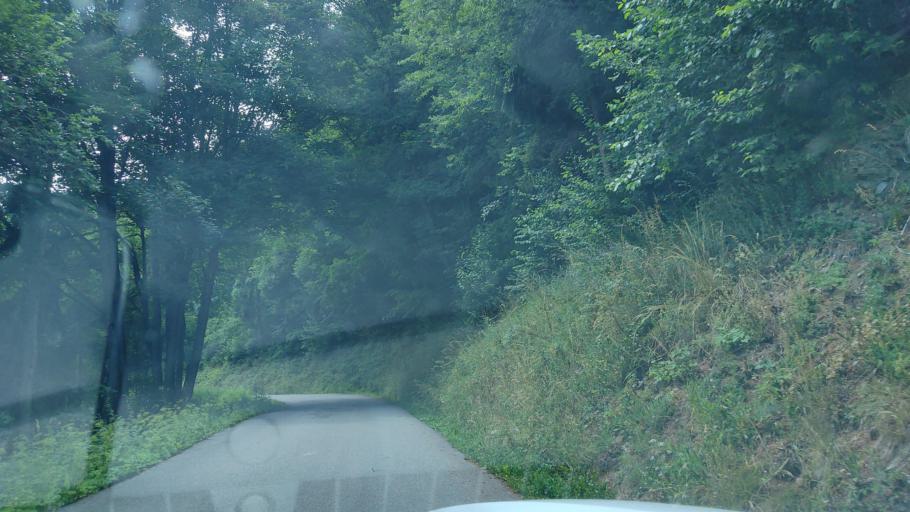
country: FR
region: Rhone-Alpes
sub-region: Departement de la Savoie
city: Beaufort
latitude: 45.7342
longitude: 6.5257
